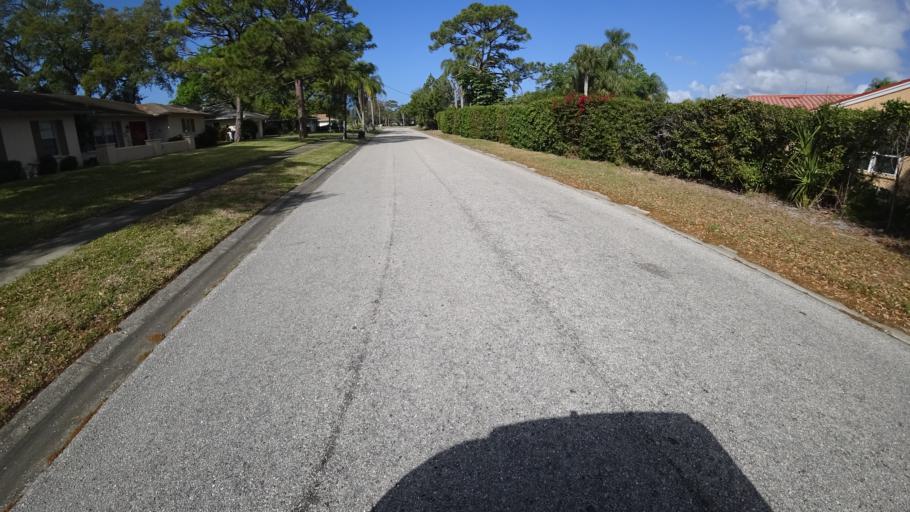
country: US
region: Florida
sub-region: Manatee County
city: Whitfield
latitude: 27.4116
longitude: -82.5654
